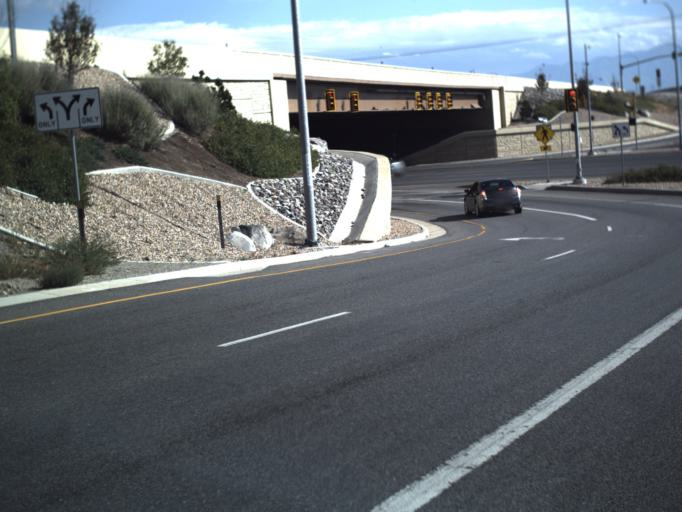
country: US
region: Utah
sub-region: Utah County
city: Lehi
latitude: 40.3891
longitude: -111.8347
